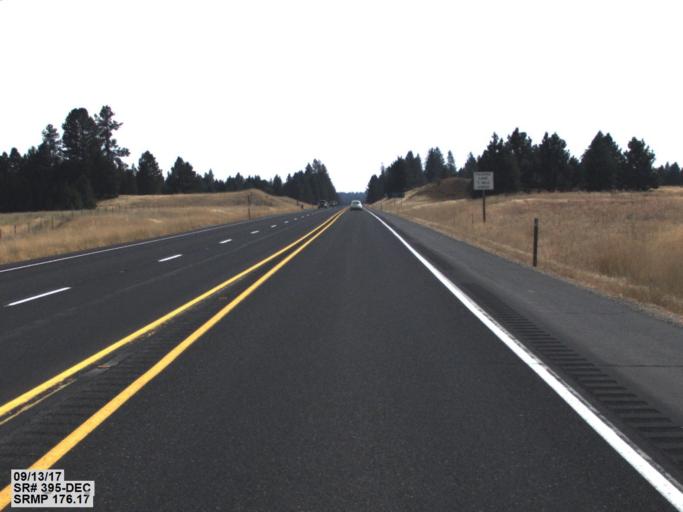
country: US
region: Washington
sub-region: Spokane County
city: Deer Park
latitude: 47.9021
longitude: -117.4384
